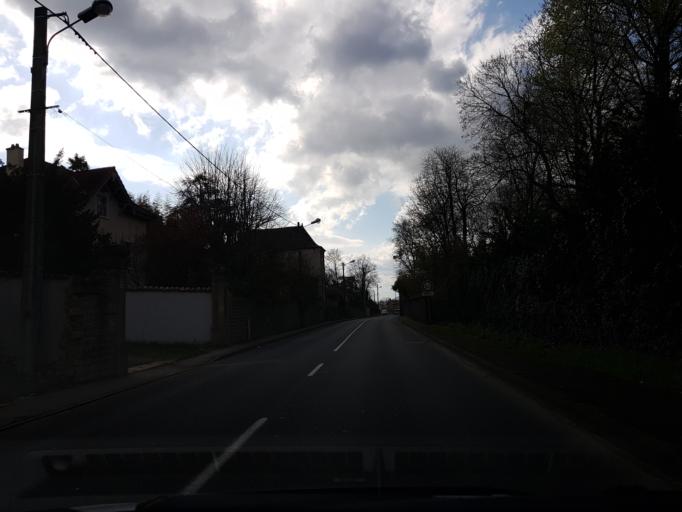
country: FR
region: Rhone-Alpes
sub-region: Departement de l'Ain
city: Trevoux
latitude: 45.9443
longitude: 4.7611
